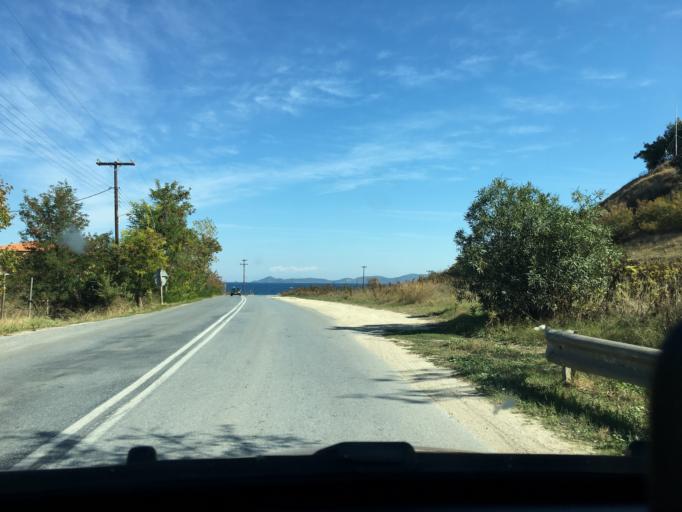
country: GR
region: Central Macedonia
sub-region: Nomos Chalkidikis
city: Ierissos
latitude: 40.3956
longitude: 23.8837
